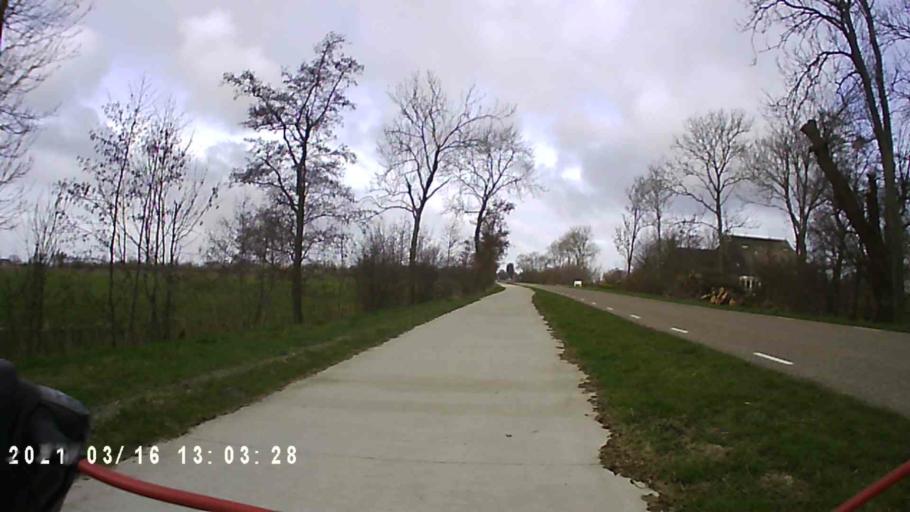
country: NL
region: Friesland
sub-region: Menameradiel
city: Berltsum
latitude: 53.2494
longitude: 5.6364
